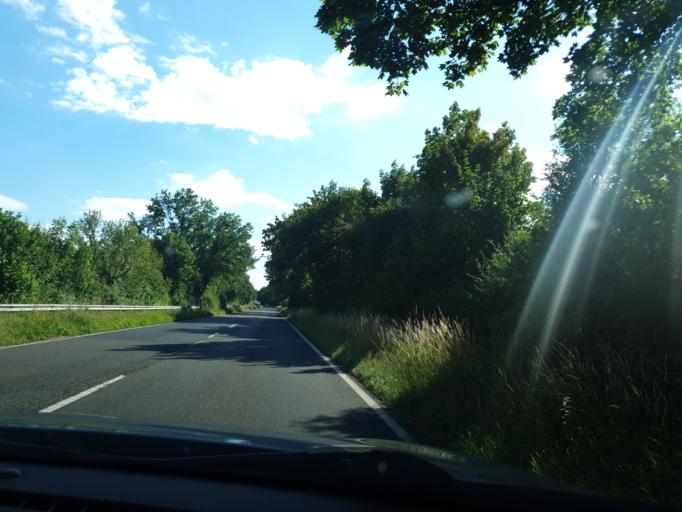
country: DE
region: North Rhine-Westphalia
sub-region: Regierungsbezirk Koln
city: Wachtberg
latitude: 50.6301
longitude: 7.1397
